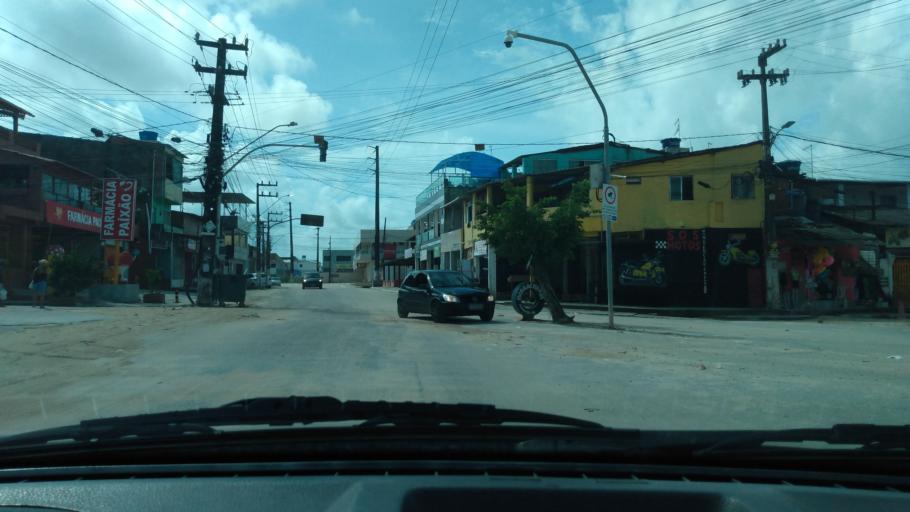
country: BR
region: Pernambuco
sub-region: Cabo De Santo Agostinho
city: Cabo
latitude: -8.3372
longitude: -34.9539
